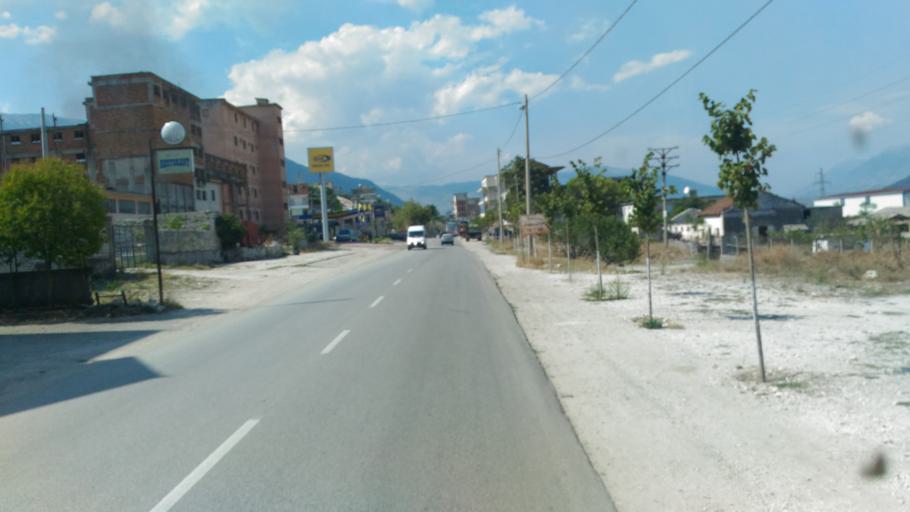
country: AL
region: Gjirokaster
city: Gjirokaster
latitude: 40.0729
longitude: 20.1566
